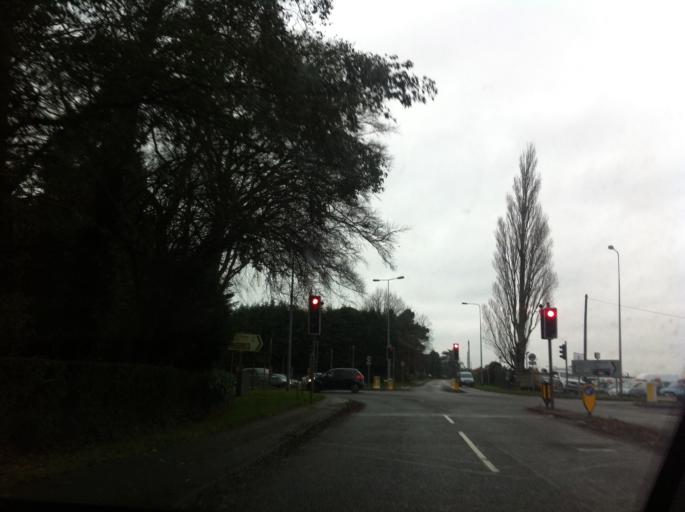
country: GB
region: England
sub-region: Northamptonshire
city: Earls Barton
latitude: 52.2619
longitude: -0.7100
